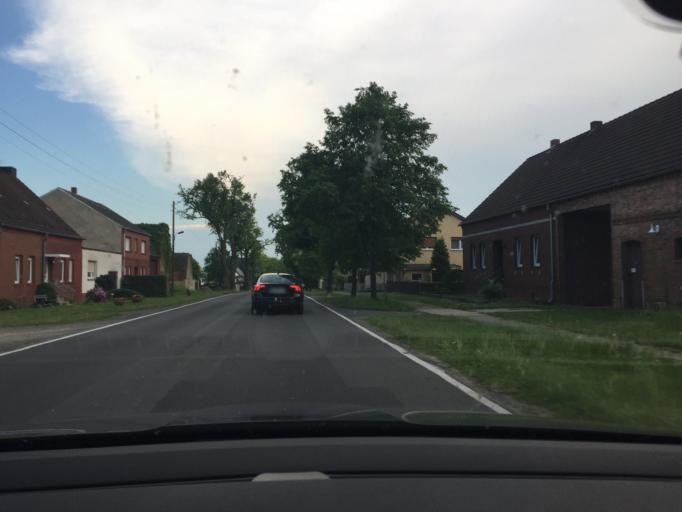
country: DE
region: Brandenburg
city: Treuenbrietzen
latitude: 52.0361
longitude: 12.8060
